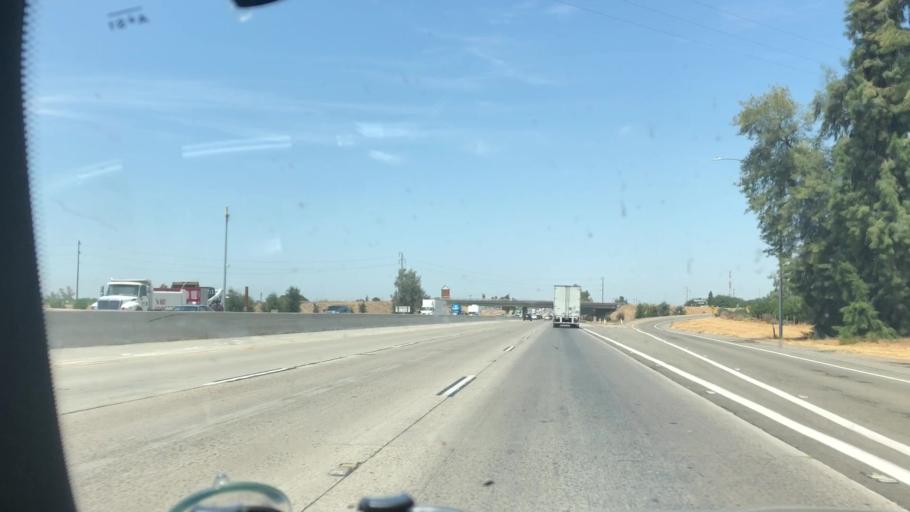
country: US
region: California
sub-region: Fresno County
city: Kingsburg
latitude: 36.5274
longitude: -119.5728
